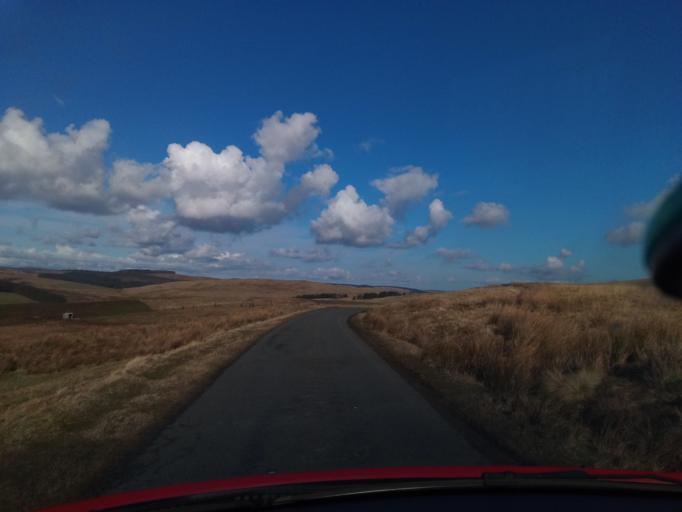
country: GB
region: Scotland
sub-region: The Scottish Borders
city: Hawick
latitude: 55.4492
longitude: -2.8859
